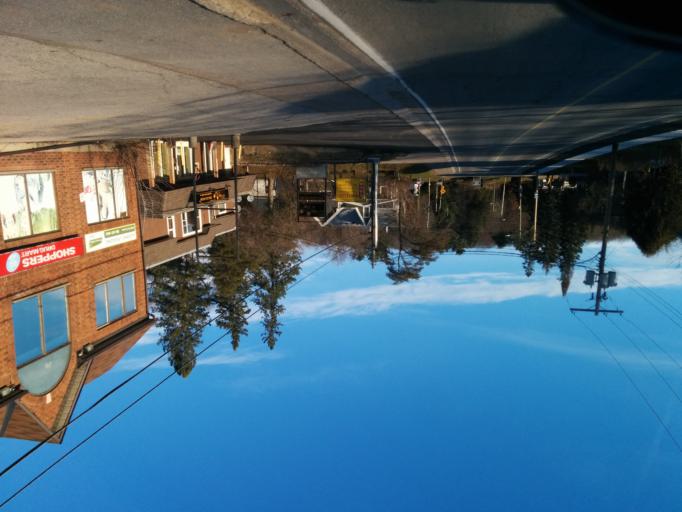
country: CA
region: Ontario
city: Bancroft
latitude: 45.0486
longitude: -78.5098
